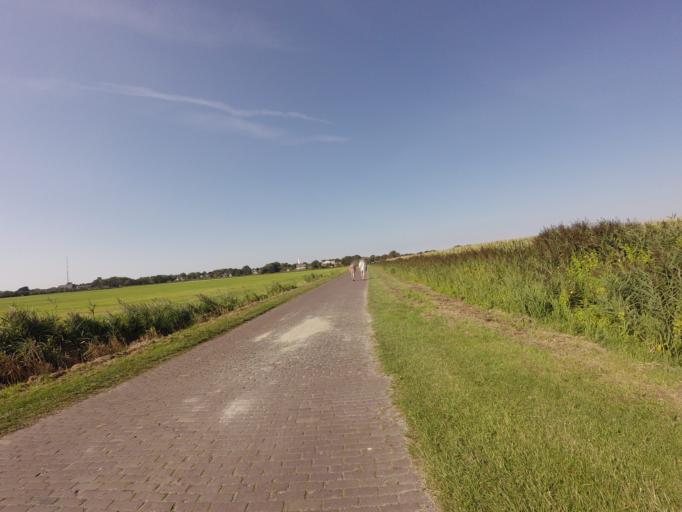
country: NL
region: Friesland
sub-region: Gemeente Schiermonnikoog
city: Schiermonnikoog
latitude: 53.4726
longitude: 6.1615
